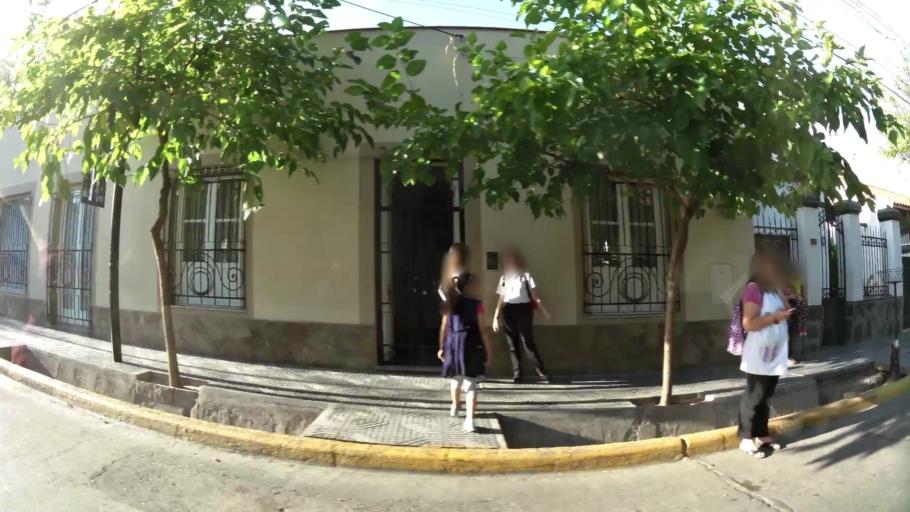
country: AR
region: Mendoza
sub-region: Departamento de Godoy Cruz
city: Godoy Cruz
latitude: -32.9081
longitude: -68.8451
